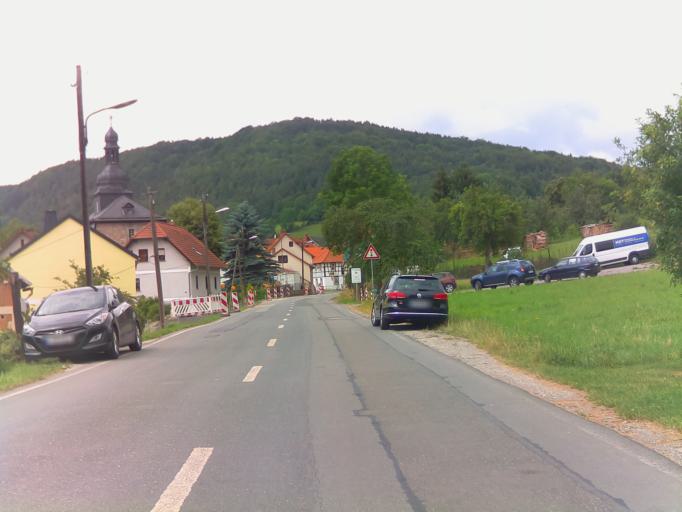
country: DE
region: Thuringia
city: Bad Blankenburg
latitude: 50.7177
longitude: 11.2767
